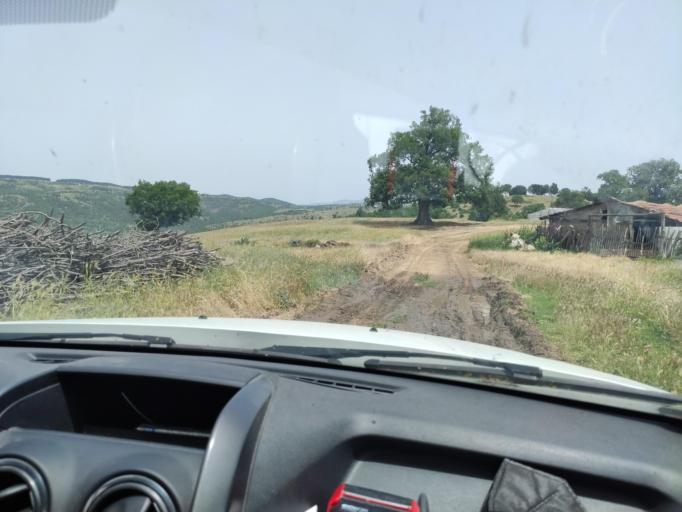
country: MK
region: Radovis
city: Radovish
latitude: 41.6780
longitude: 22.4004
